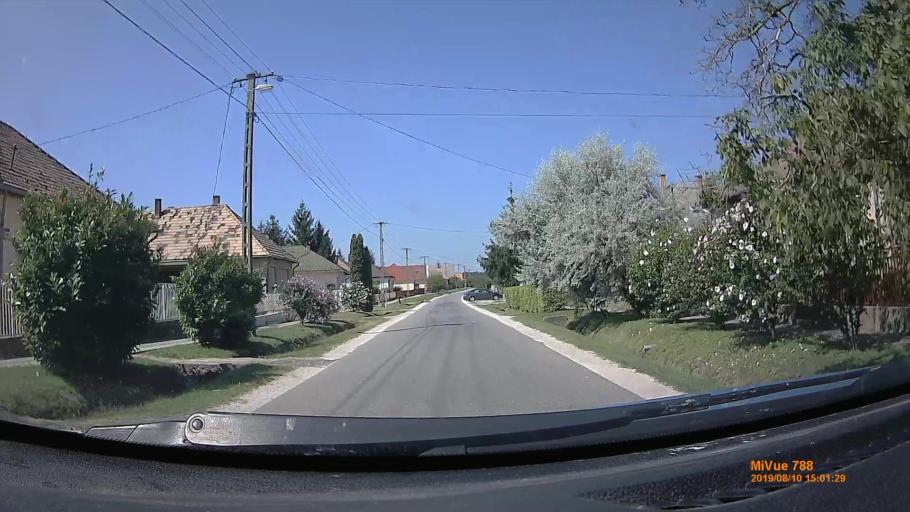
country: HU
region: Somogy
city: Lengyeltoti
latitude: 46.6496
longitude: 17.5771
